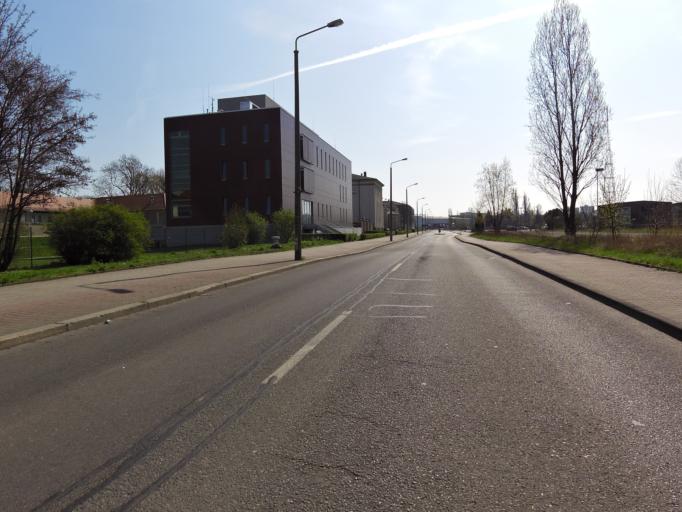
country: DE
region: Saxony
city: Leipzig
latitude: 51.3210
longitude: 12.3902
